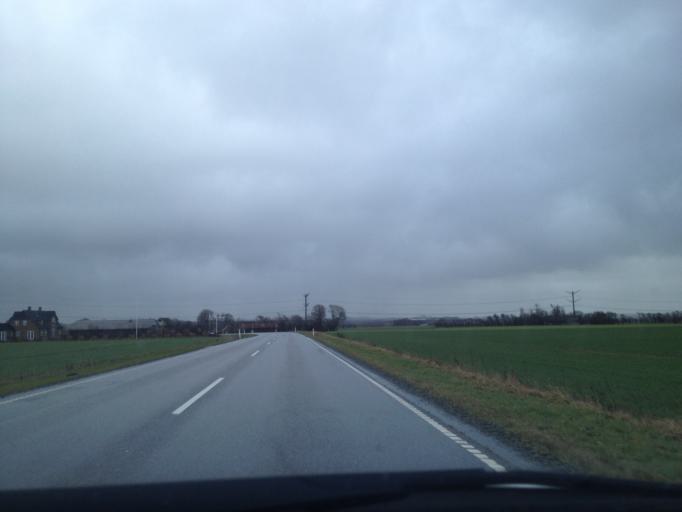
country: DK
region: South Denmark
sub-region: Vejen Kommune
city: Rodding
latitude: 55.3578
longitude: 9.1541
